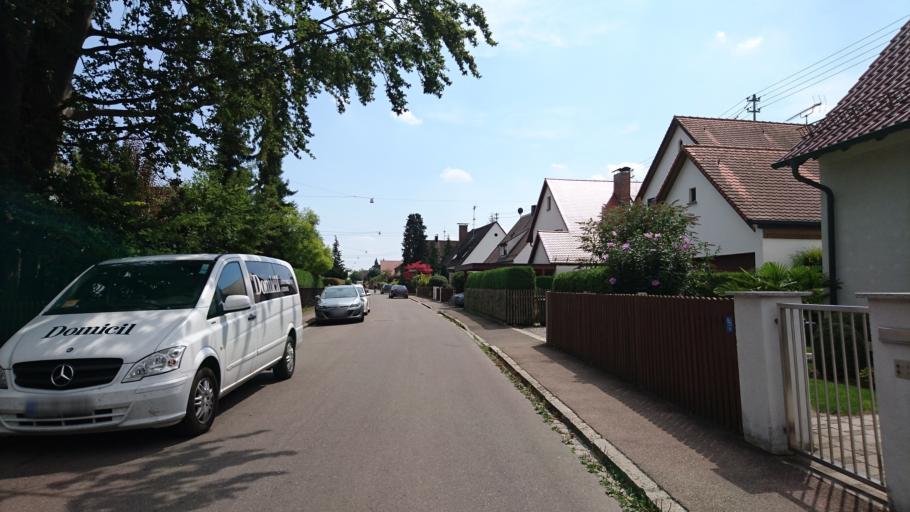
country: DE
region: Bavaria
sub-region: Swabia
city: Augsburg
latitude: 48.3896
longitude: 10.9243
